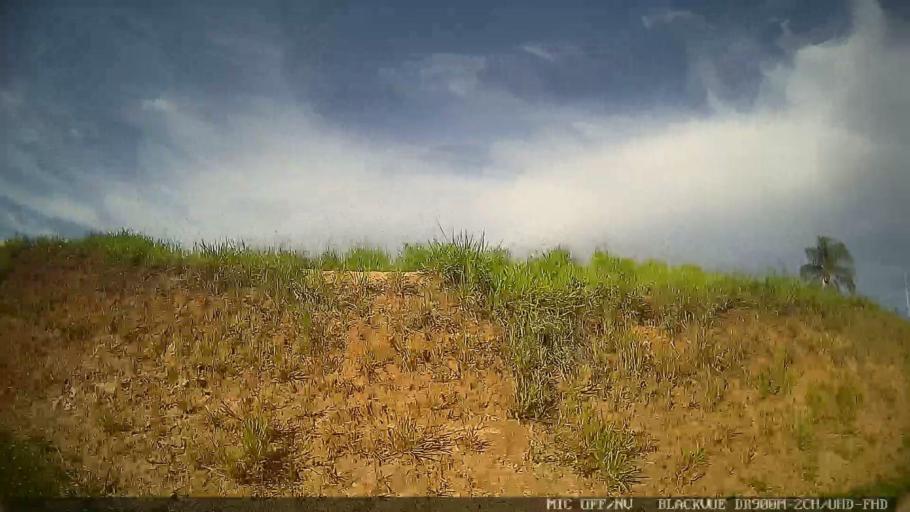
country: BR
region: Sao Paulo
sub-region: Tiete
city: Tiete
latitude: -23.1216
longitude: -47.7014
